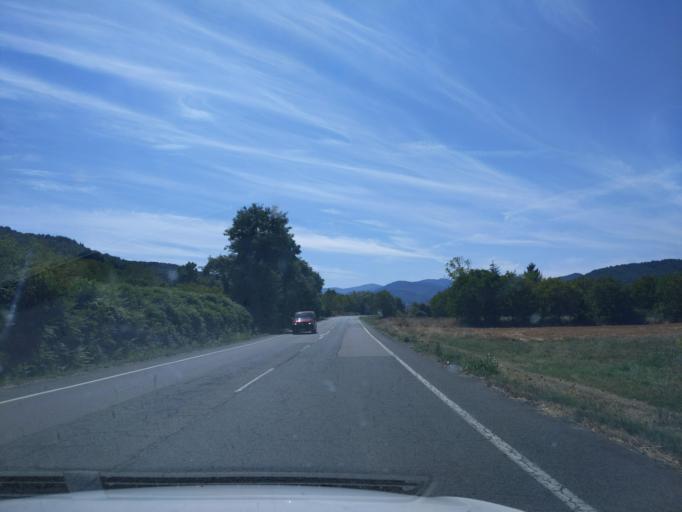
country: ES
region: La Rioja
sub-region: Provincia de La Rioja
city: Ojacastro
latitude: 42.3668
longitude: -2.9828
